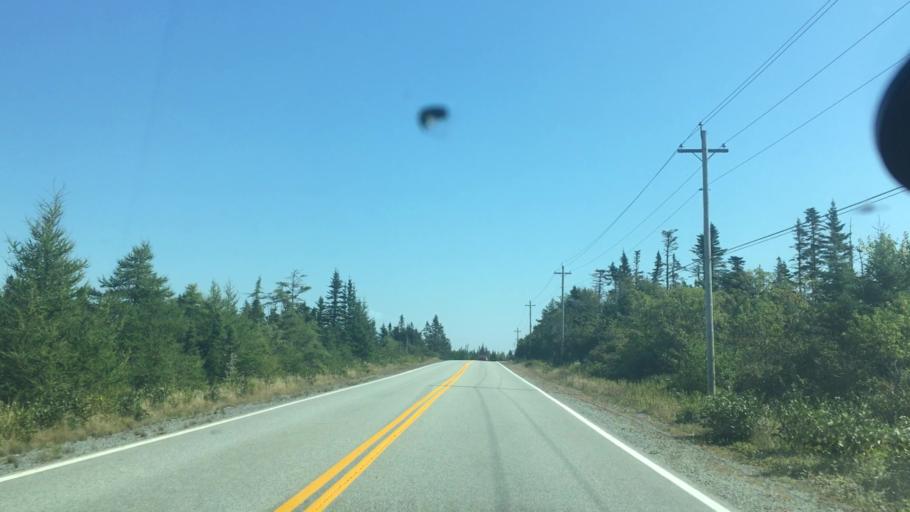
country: CA
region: Nova Scotia
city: Antigonish
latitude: 44.9333
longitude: -62.2845
